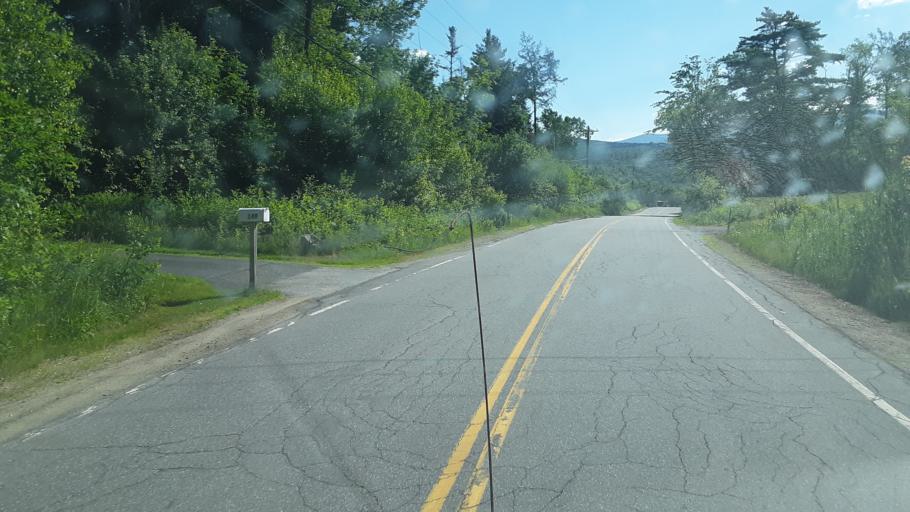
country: US
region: New Hampshire
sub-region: Grafton County
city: North Haverhill
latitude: 44.1025
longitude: -71.9064
